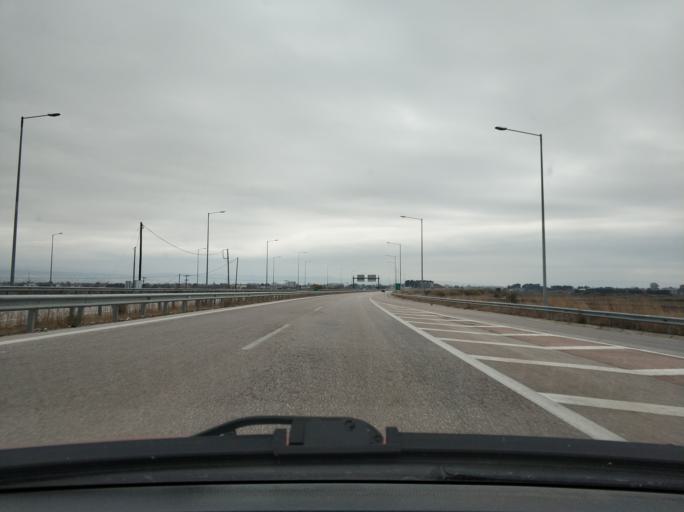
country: GR
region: Central Macedonia
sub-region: Nomos Thessalonikis
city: Lagyna
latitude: 40.7391
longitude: 23.0154
